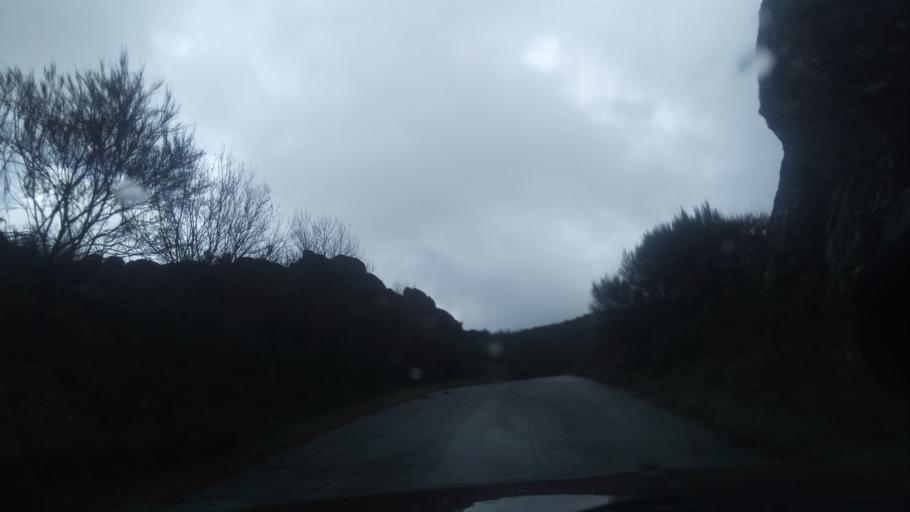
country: PT
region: Guarda
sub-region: Celorico da Beira
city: Celorico da Beira
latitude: 40.5233
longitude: -7.4531
